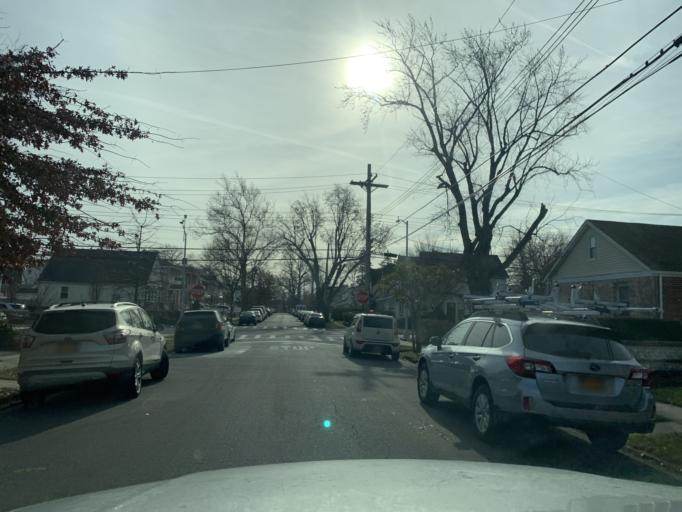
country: US
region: New York
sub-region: Queens County
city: Jamaica
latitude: 40.6911
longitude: -73.7757
